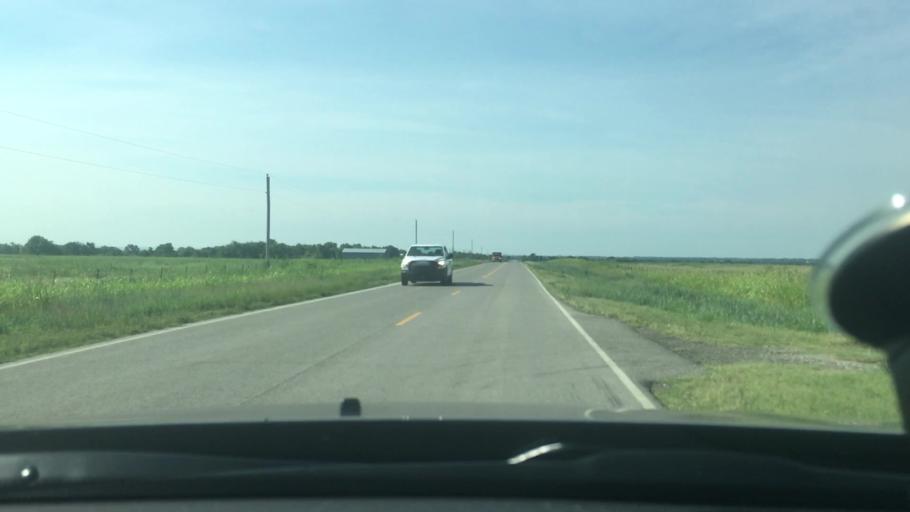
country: US
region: Oklahoma
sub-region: Garvin County
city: Maysville
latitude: 34.6650
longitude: -97.4053
